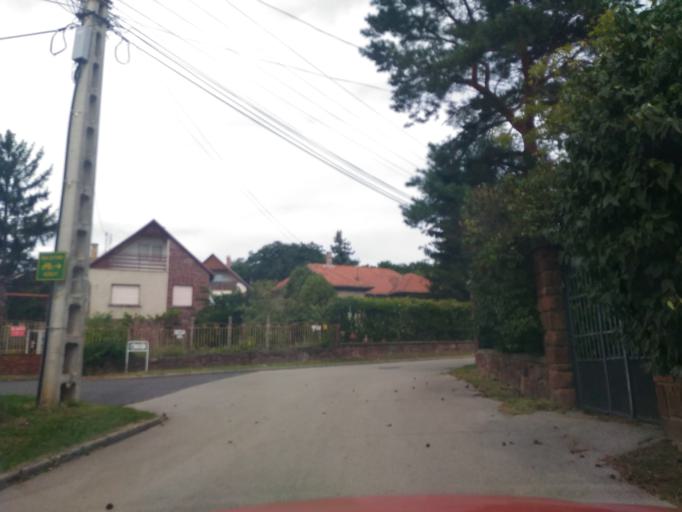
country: HU
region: Veszprem
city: Zanka
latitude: 46.8539
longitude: 17.6633
